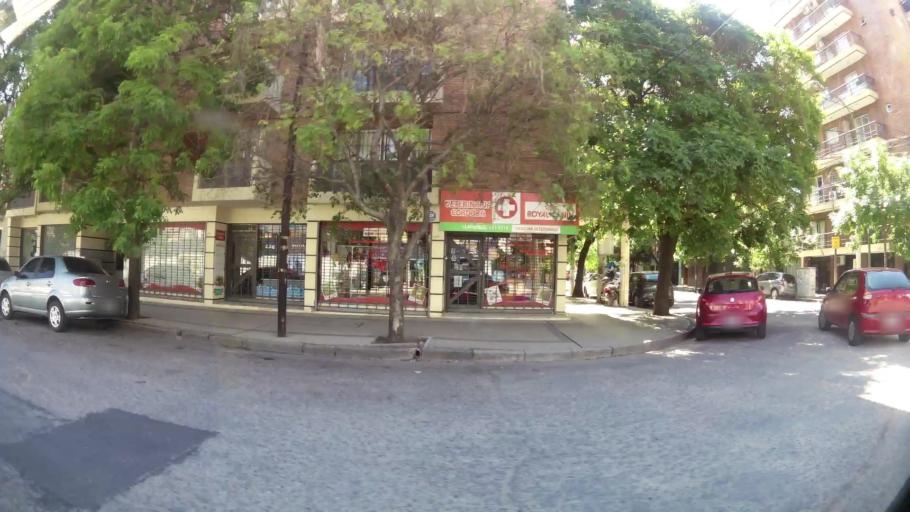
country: AR
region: Cordoba
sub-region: Departamento de Capital
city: Cordoba
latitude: -31.3988
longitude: -64.1842
